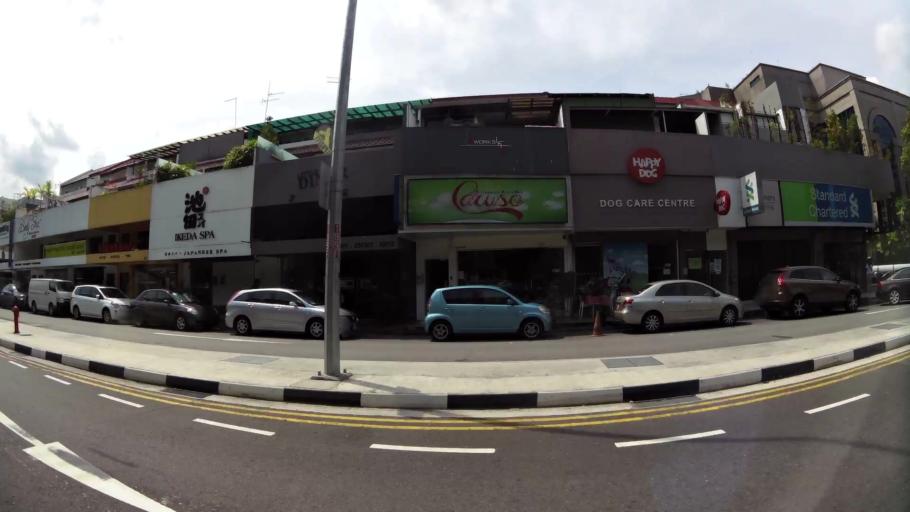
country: SG
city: Singapore
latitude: 1.3313
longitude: 103.7963
